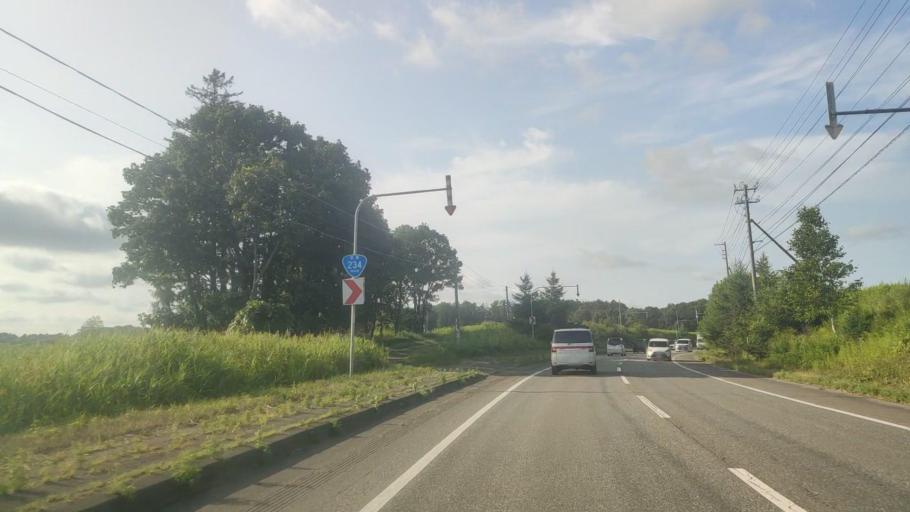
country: JP
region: Hokkaido
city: Chitose
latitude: 42.8025
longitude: 141.8344
